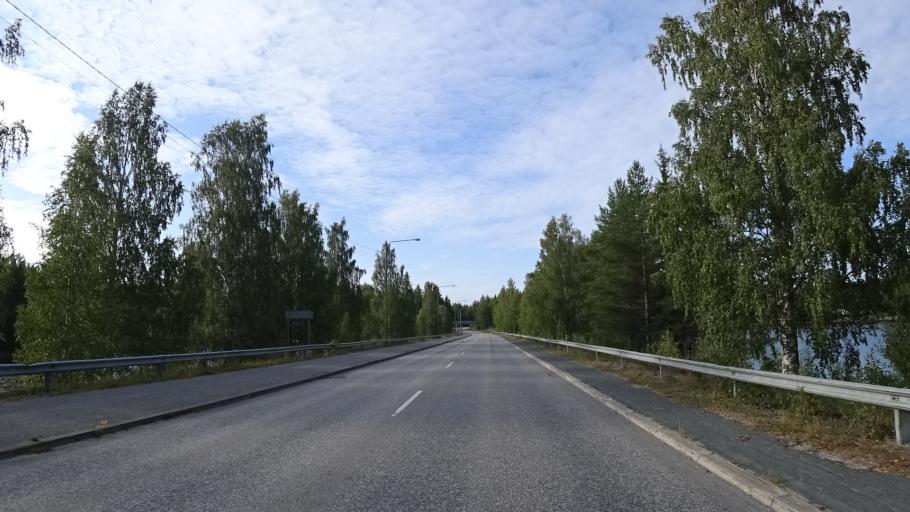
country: FI
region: North Karelia
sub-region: Joensuu
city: Eno
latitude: 62.8042
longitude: 30.1529
